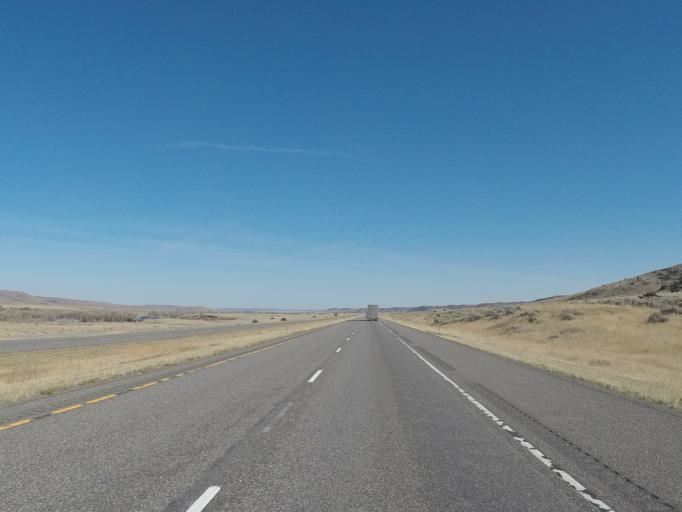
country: US
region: Montana
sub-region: Sweet Grass County
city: Big Timber
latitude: 45.7416
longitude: -110.1964
